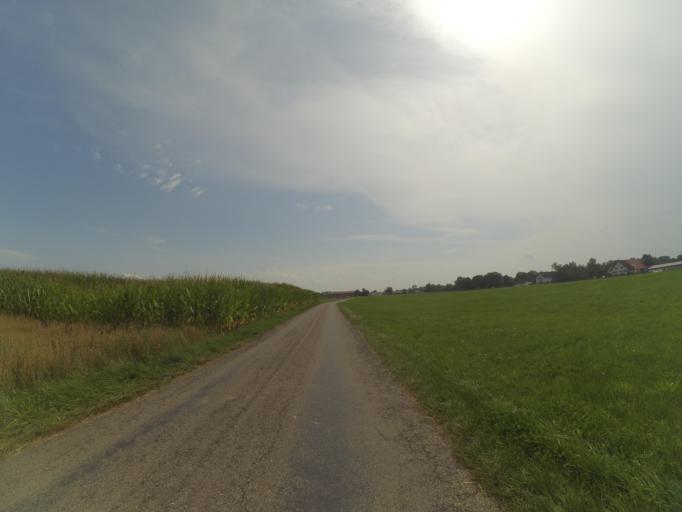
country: DE
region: Bavaria
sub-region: Swabia
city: Jengen
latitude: 48.0098
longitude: 10.7268
